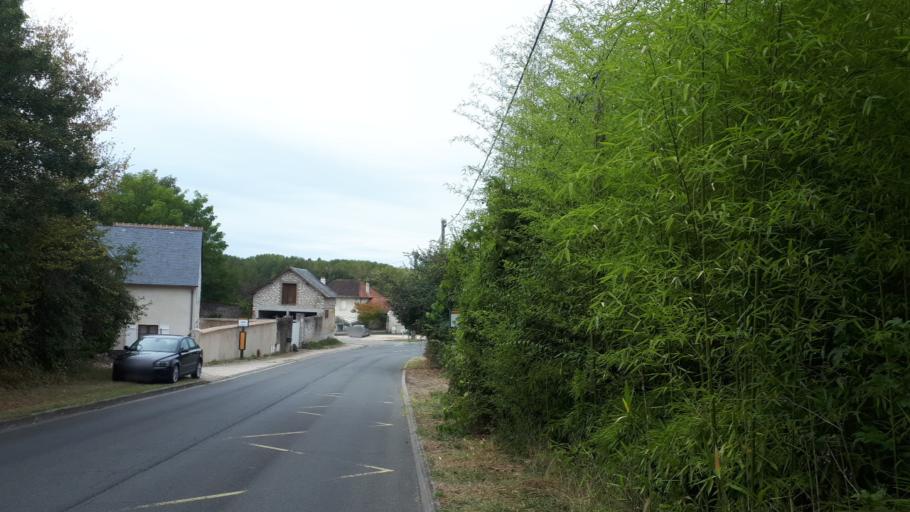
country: FR
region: Centre
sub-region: Departement du Loir-et-Cher
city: Saint-Gervais-la-Foret
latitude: 47.5669
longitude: 1.3484
